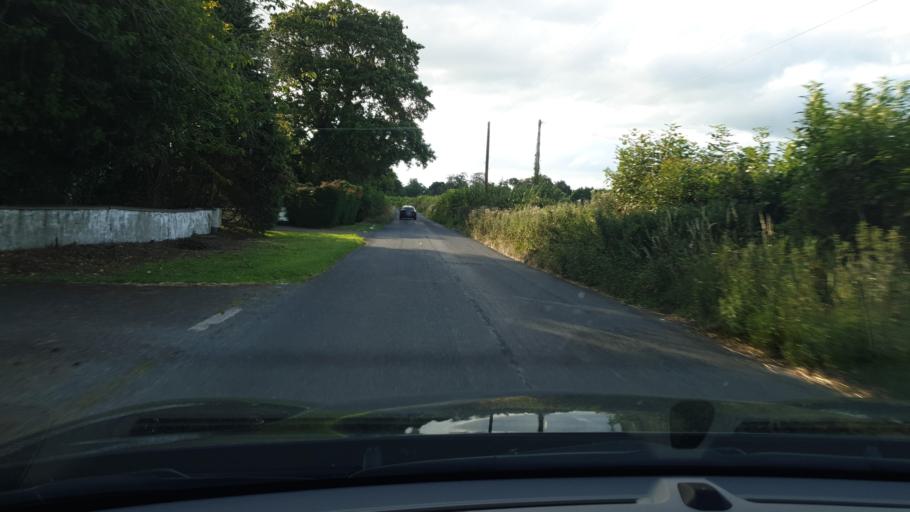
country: IE
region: Leinster
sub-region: Lu
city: Drogheda
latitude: 53.6901
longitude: -6.3398
